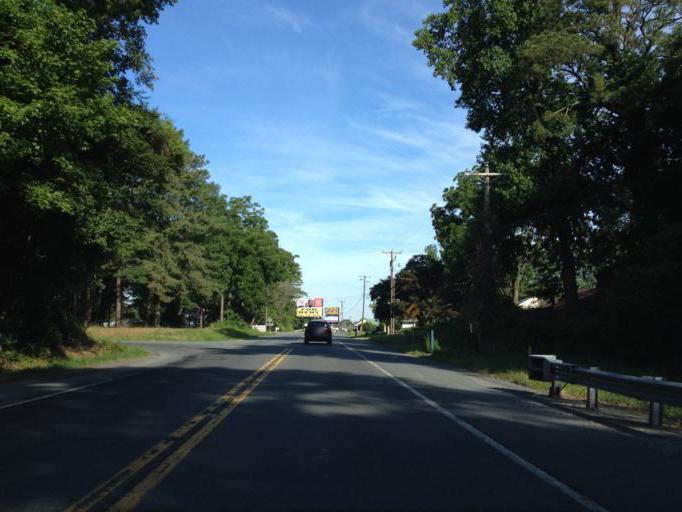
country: US
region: Delaware
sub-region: Sussex County
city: Millsboro
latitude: 38.5643
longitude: -75.2742
